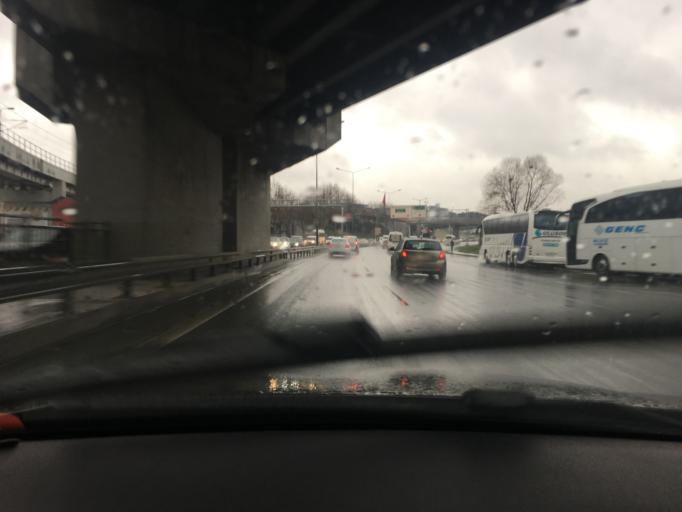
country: TR
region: Istanbul
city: Esenler
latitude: 41.0367
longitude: 28.8916
